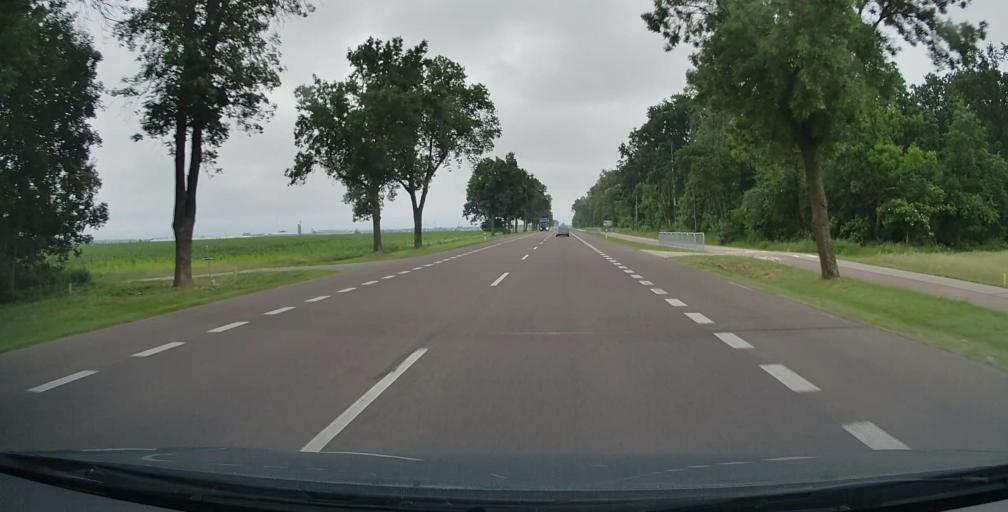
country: PL
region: Lublin Voivodeship
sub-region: Powiat bialski
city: Rzeczyca
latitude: 52.0123
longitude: 22.7374
